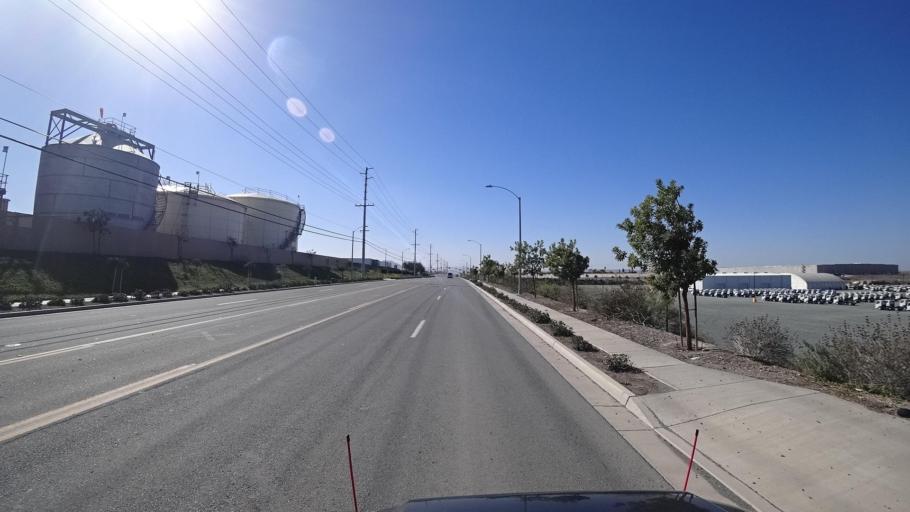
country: MX
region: Baja California
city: Tijuana
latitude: 32.5740
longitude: -116.9192
